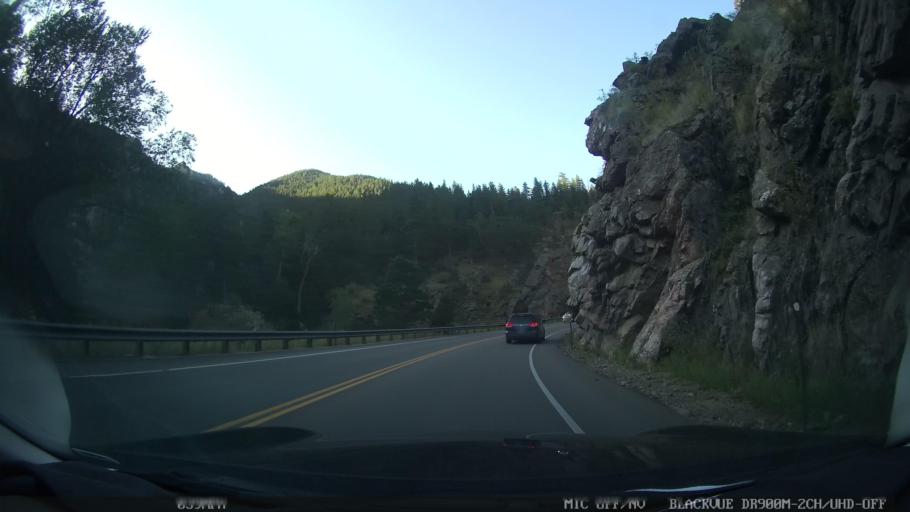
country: US
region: Colorado
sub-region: Larimer County
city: Estes Park
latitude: 40.4289
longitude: -105.3391
